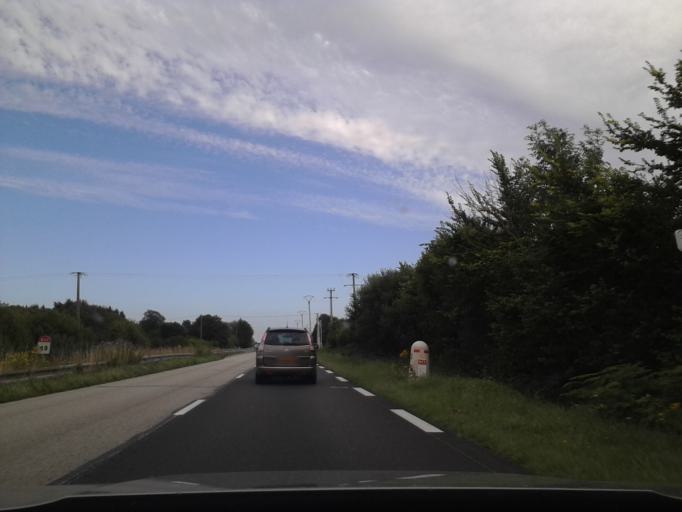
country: FR
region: Lower Normandy
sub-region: Departement de la Manche
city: Brix
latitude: 49.5741
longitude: -1.5783
